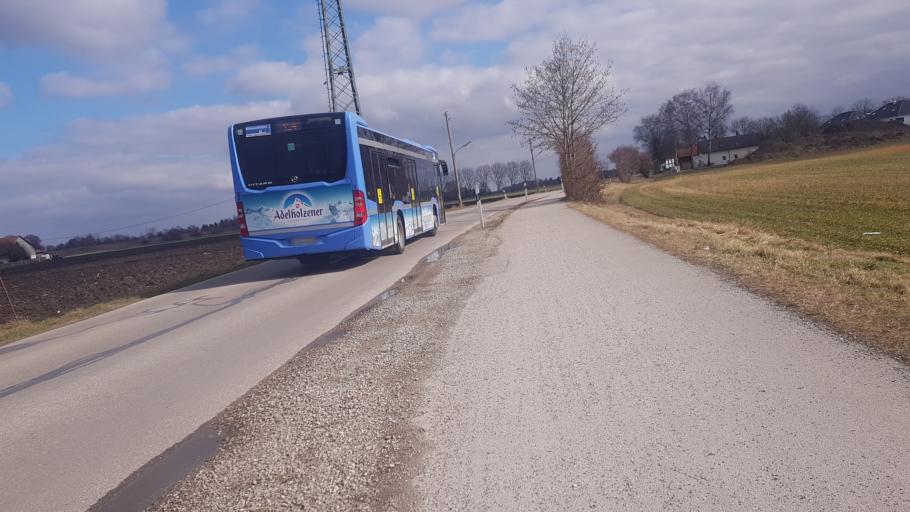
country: DE
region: Bavaria
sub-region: Upper Bavaria
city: Unterfoehring
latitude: 48.1696
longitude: 11.6537
